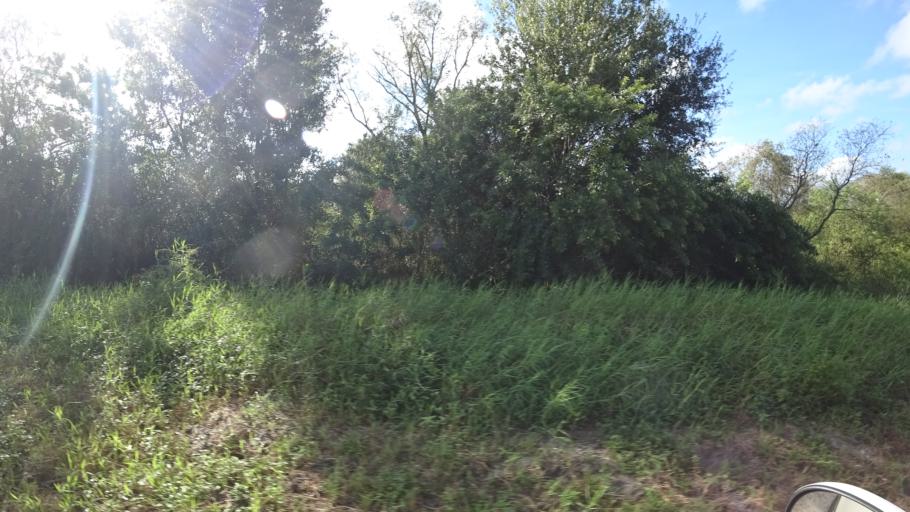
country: US
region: Florida
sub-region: Hillsborough County
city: Wimauma
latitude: 27.5566
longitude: -82.3201
